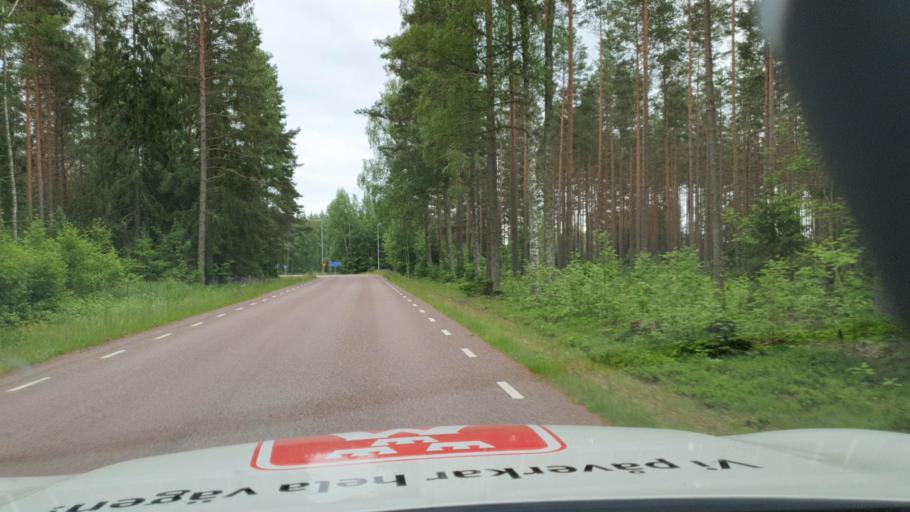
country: SE
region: Vaermland
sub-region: Forshaga Kommun
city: Forshaga
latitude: 59.4836
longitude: 13.4107
